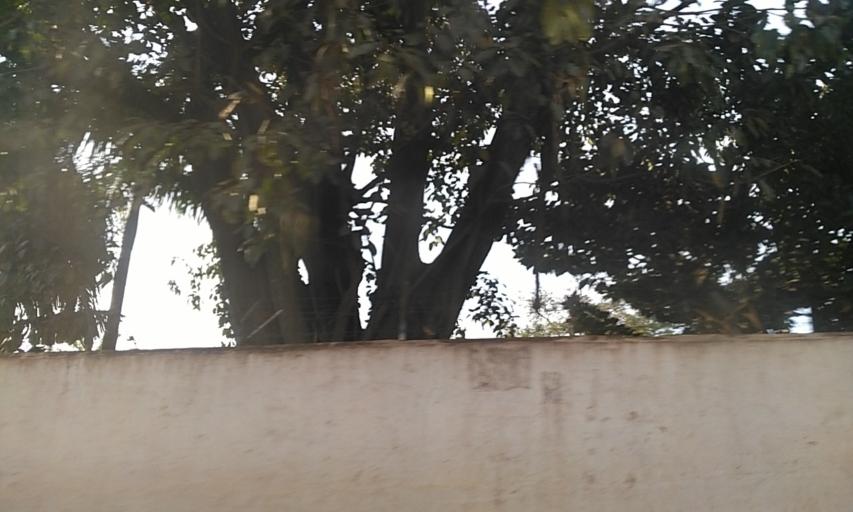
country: UG
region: Central Region
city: Kampala Central Division
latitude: 0.3218
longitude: 32.5732
